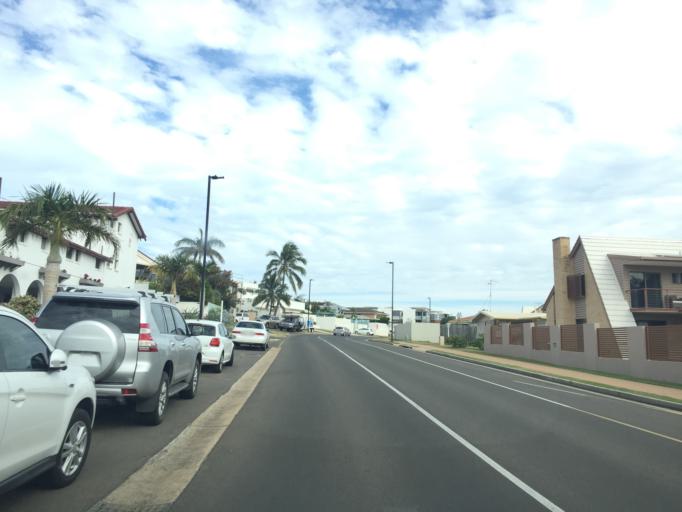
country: AU
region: Queensland
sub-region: Bundaberg
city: Bundaberg
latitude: -24.8212
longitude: 152.4649
